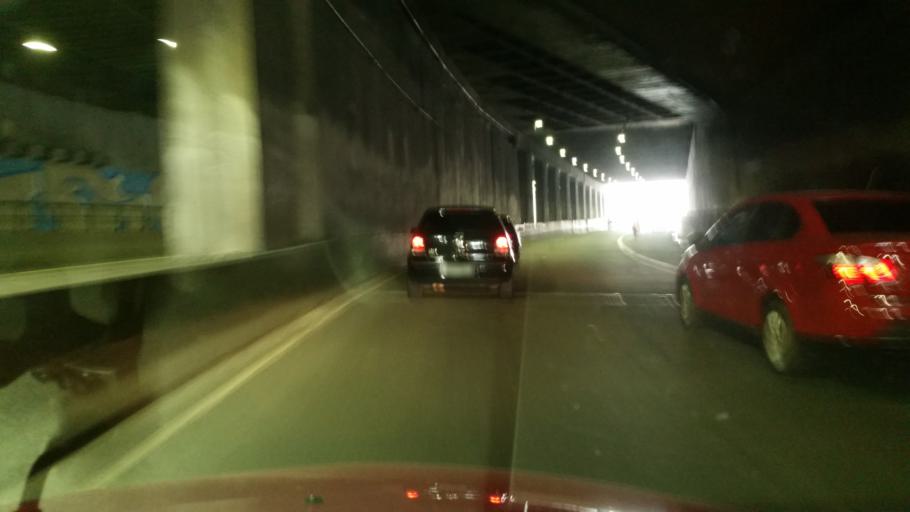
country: BR
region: Sao Paulo
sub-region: Ferraz De Vasconcelos
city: Ferraz de Vasconcelos
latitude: -23.5413
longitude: -46.4656
